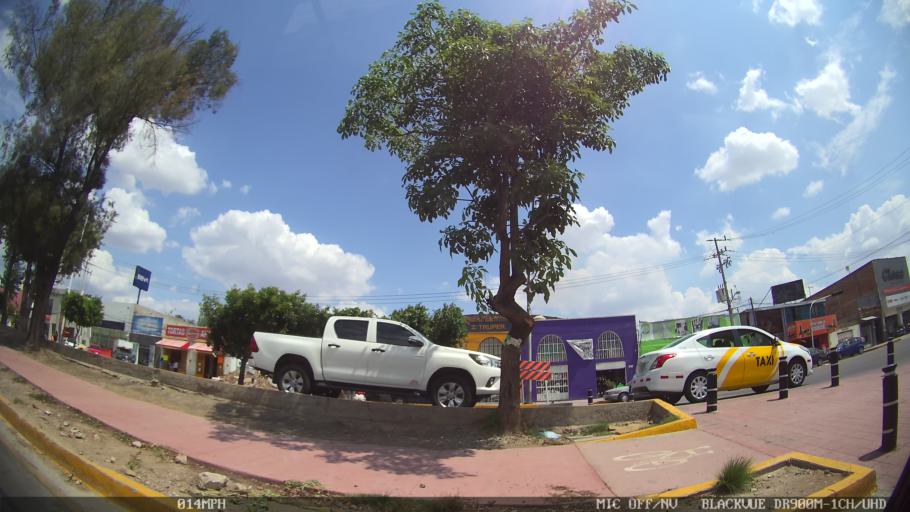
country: MX
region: Jalisco
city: Tonala
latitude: 20.6187
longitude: -103.2520
